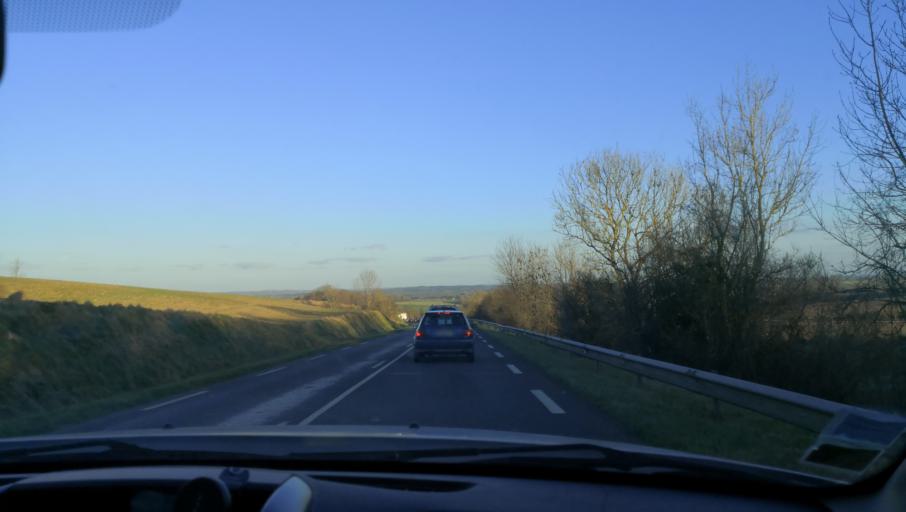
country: FR
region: Haute-Normandie
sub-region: Departement de la Seine-Maritime
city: Buchy
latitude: 49.5934
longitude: 1.4471
